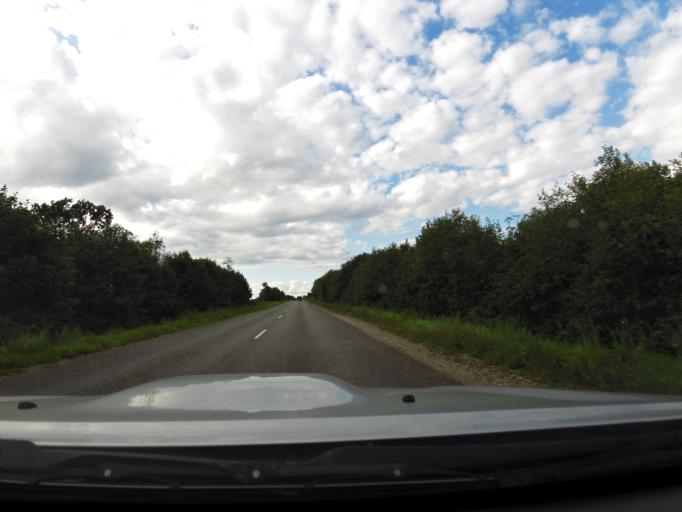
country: LV
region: Akniste
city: Akniste
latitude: 56.0184
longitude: 25.9237
